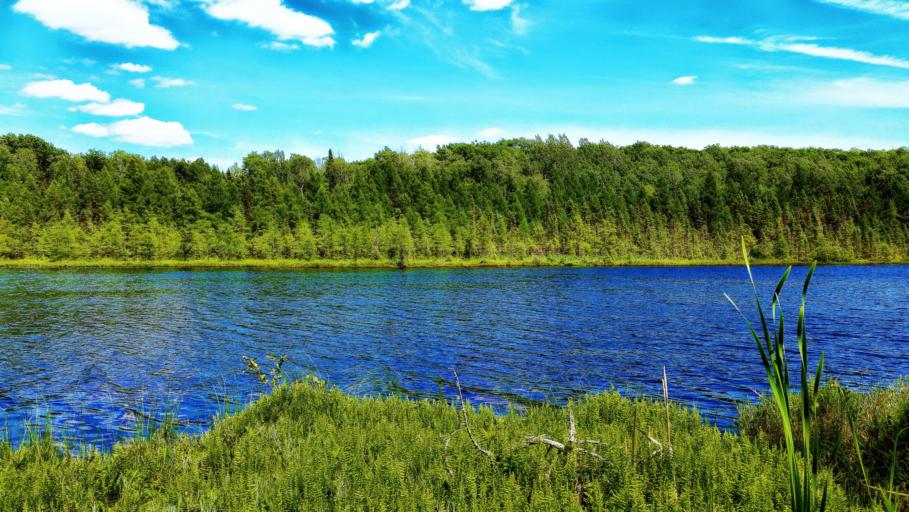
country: US
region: Wisconsin
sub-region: Sawyer County
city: Hayward
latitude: 46.0165
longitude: -91.5347
